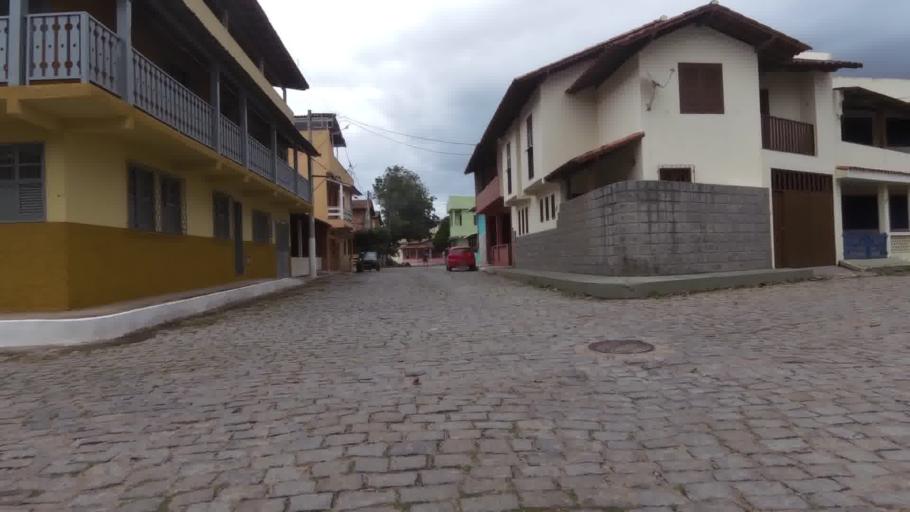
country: BR
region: Espirito Santo
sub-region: Marataizes
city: Marataizes
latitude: -21.0478
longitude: -40.8313
